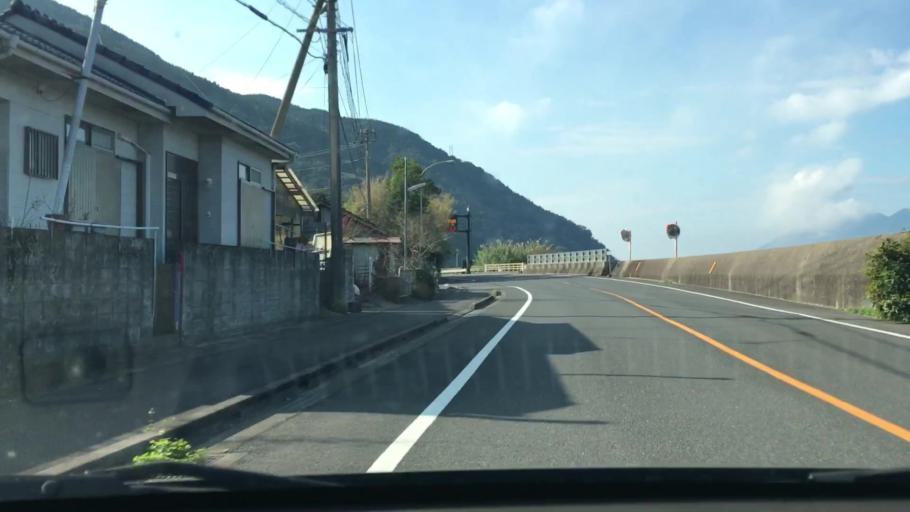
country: JP
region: Kagoshima
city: Kokubu-matsuki
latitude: 31.6484
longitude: 130.8204
